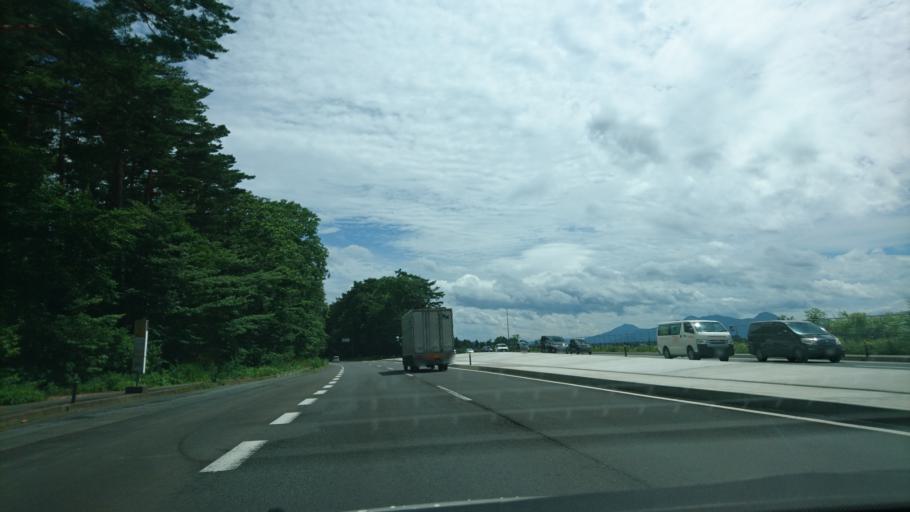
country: JP
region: Iwate
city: Morioka-shi
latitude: 39.7668
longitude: 141.1312
